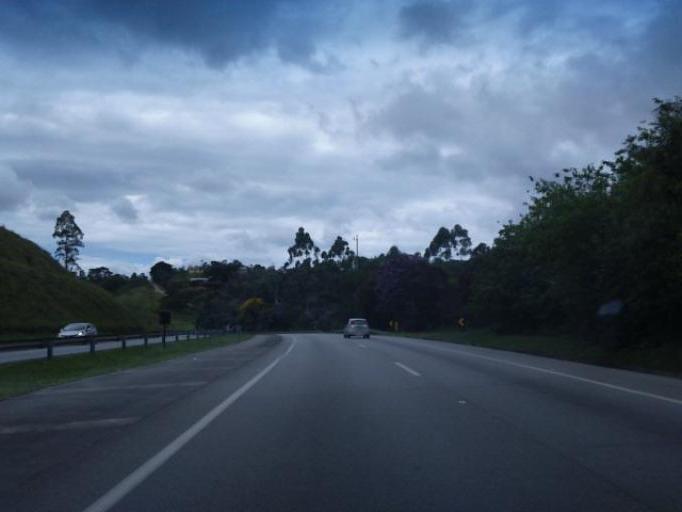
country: BR
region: Sao Paulo
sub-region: Juquitiba
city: Juquitiba
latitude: -23.9858
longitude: -47.1480
